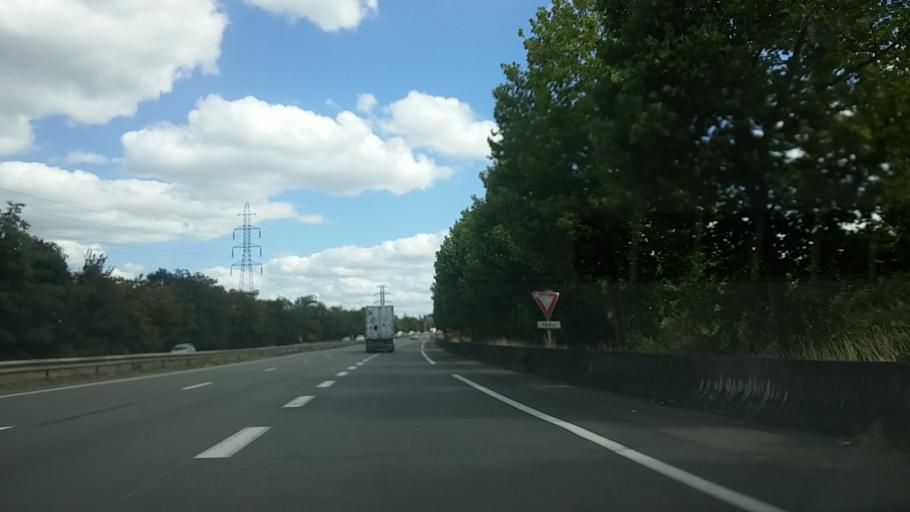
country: FR
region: Ile-de-France
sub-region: Departement des Yvelines
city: Fontenay-le-Fleury
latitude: 48.7947
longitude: 2.0485
